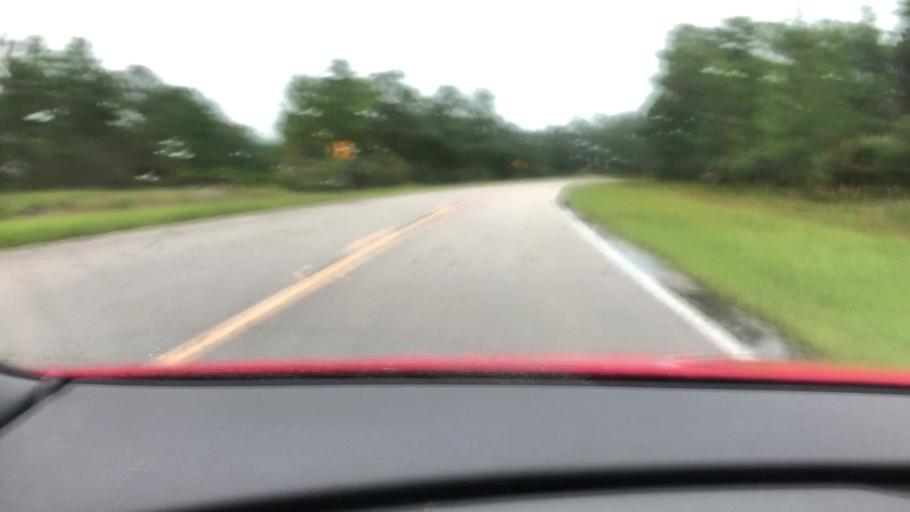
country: US
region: Florida
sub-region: Volusia County
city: Samsula-Spruce Creek
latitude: 29.0367
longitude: -81.0856
